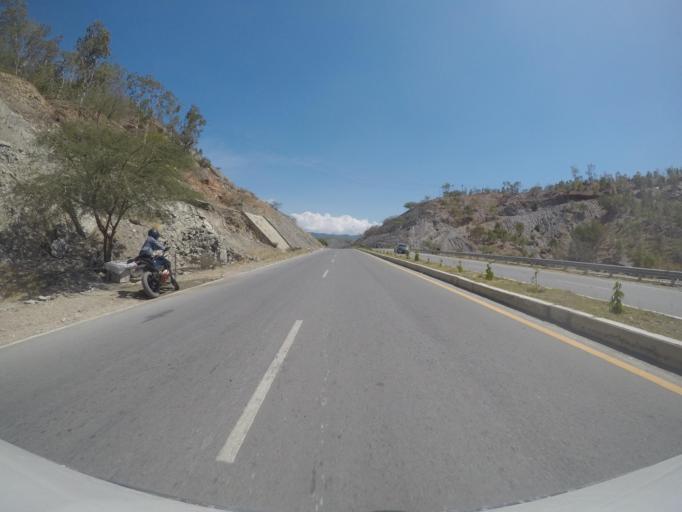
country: TL
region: Dili
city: Dili
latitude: -8.5609
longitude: 125.4937
